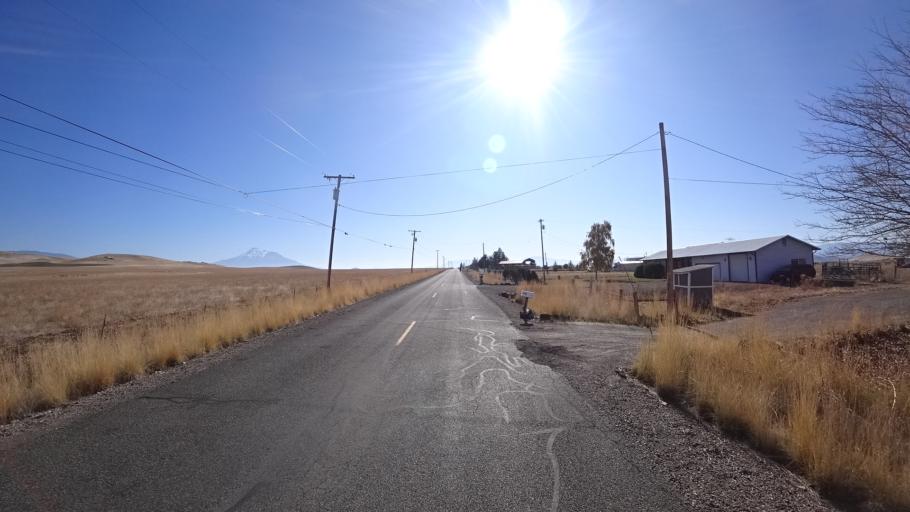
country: US
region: California
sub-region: Siskiyou County
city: Montague
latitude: 41.7525
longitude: -122.4571
